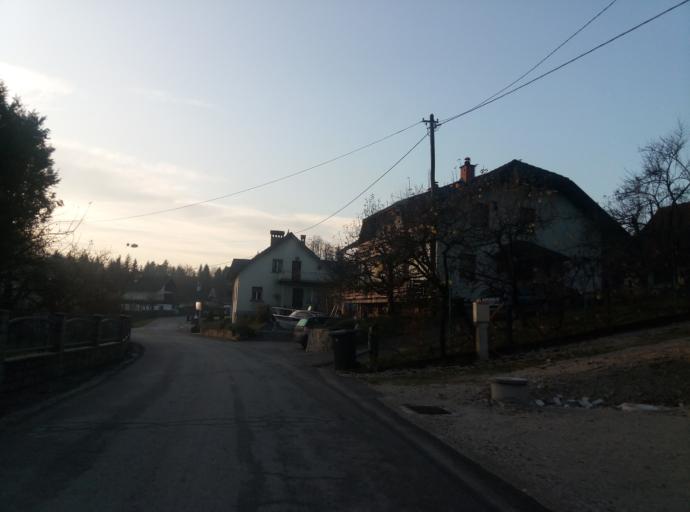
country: SI
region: Vodice
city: Vodice
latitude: 46.1702
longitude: 14.4805
